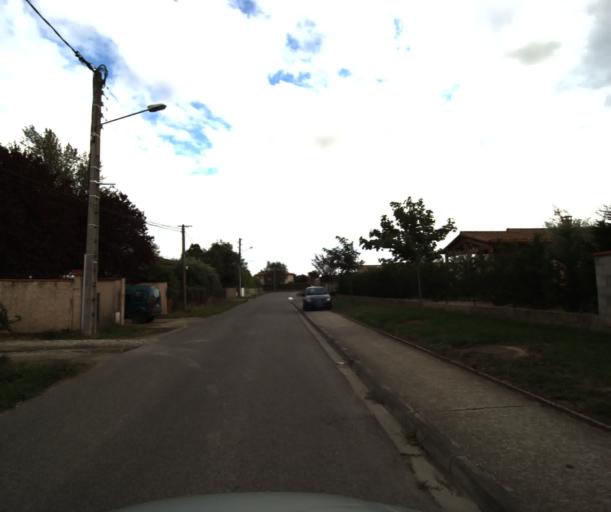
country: FR
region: Midi-Pyrenees
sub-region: Departement de la Haute-Garonne
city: Eaunes
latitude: 43.4259
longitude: 1.3482
